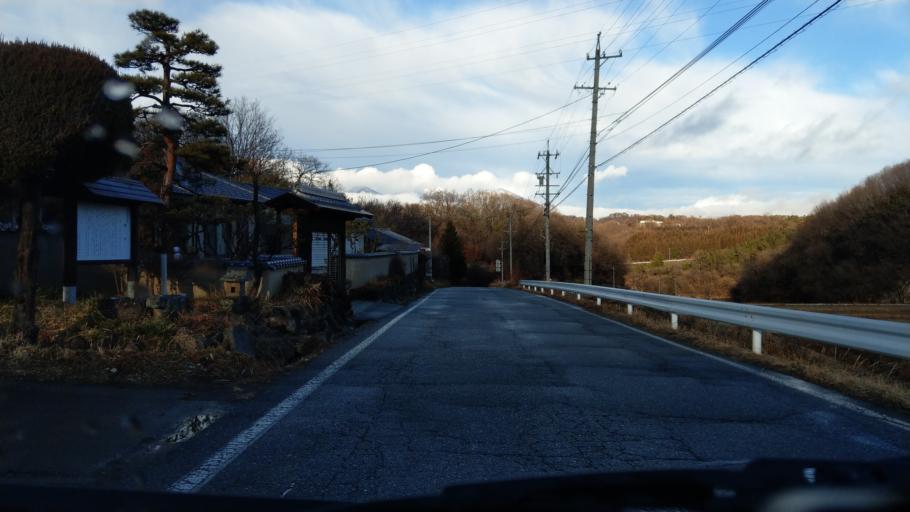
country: JP
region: Nagano
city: Kamimaruko
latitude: 36.2905
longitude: 138.3365
